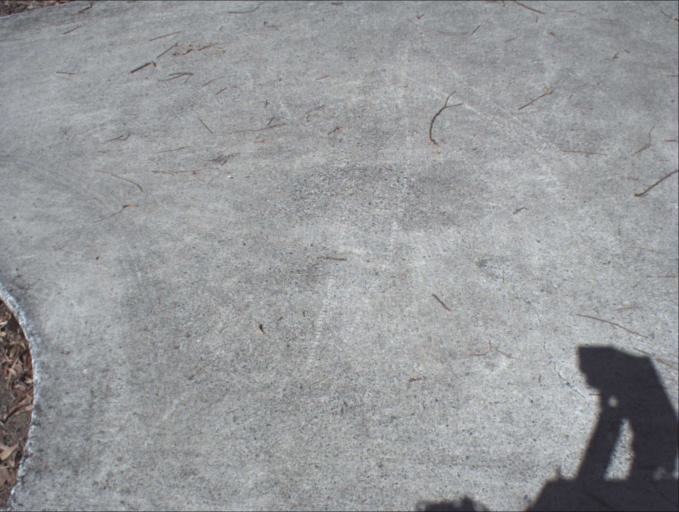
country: AU
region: Queensland
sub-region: Logan
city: Springwood
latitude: -27.5994
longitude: 153.1497
